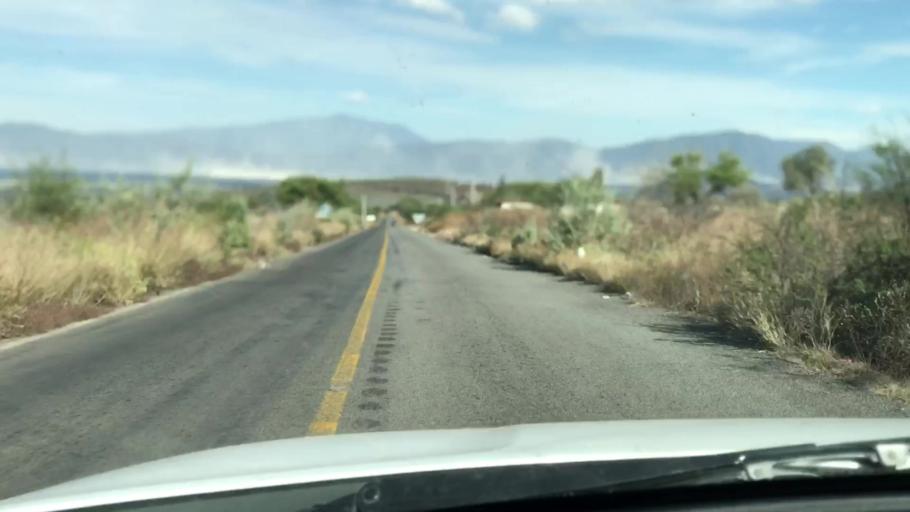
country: MX
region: Jalisco
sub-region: Zacoalco de Torres
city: Barranca de Otates (Barranca de Otatan)
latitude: 20.2569
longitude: -103.6683
